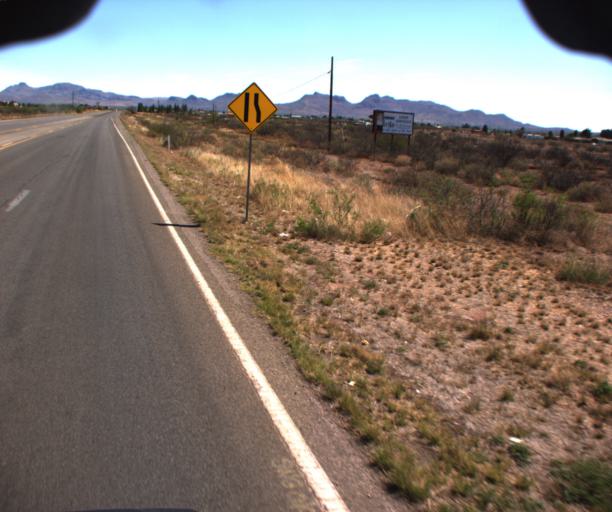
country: US
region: Arizona
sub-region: Cochise County
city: Douglas
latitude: 31.3620
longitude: -109.5447
